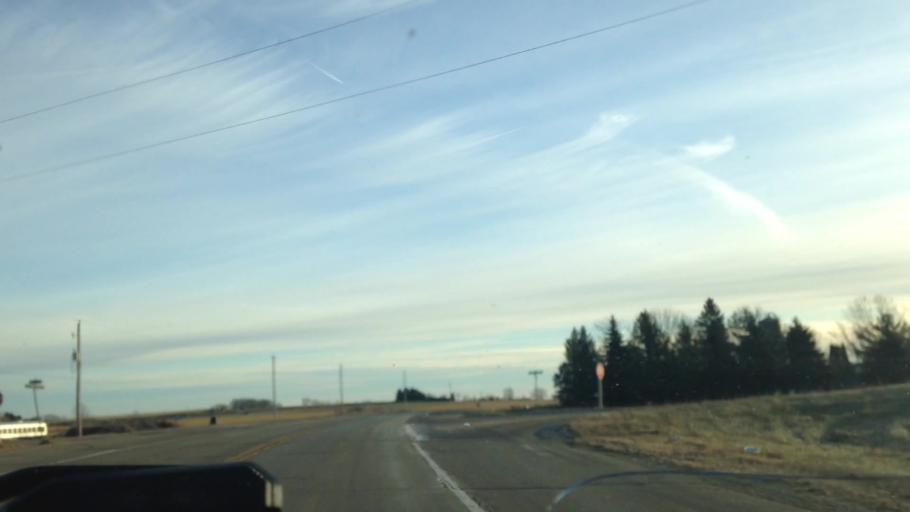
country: US
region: Wisconsin
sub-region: Dodge County
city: Mayville
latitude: 43.5150
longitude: -88.5269
